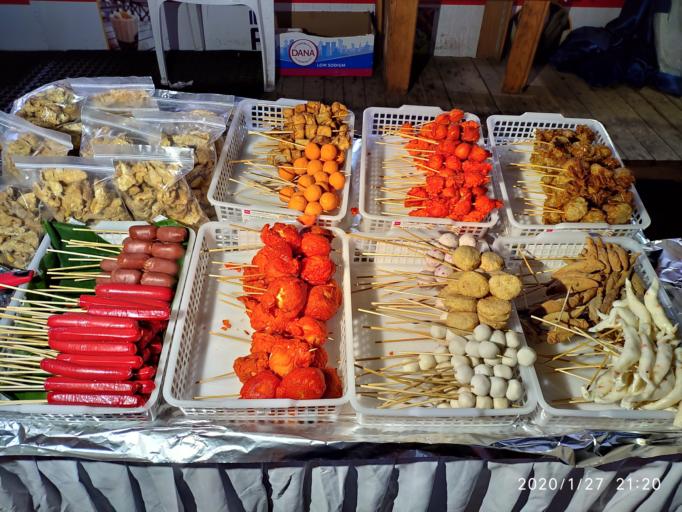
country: QA
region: Baladiyat ad Dawhah
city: Doha
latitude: 25.3213
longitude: 51.5353
